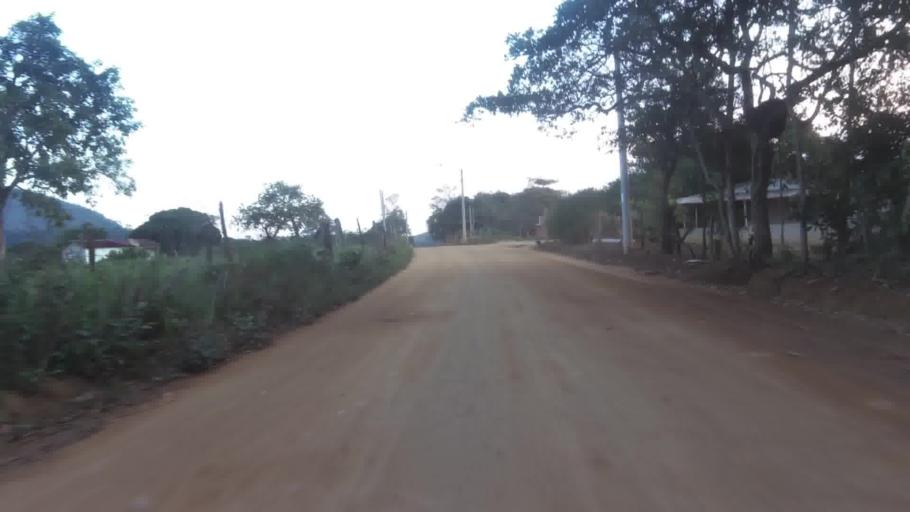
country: BR
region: Espirito Santo
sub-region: Guarapari
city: Guarapari
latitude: -20.7033
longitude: -40.5740
